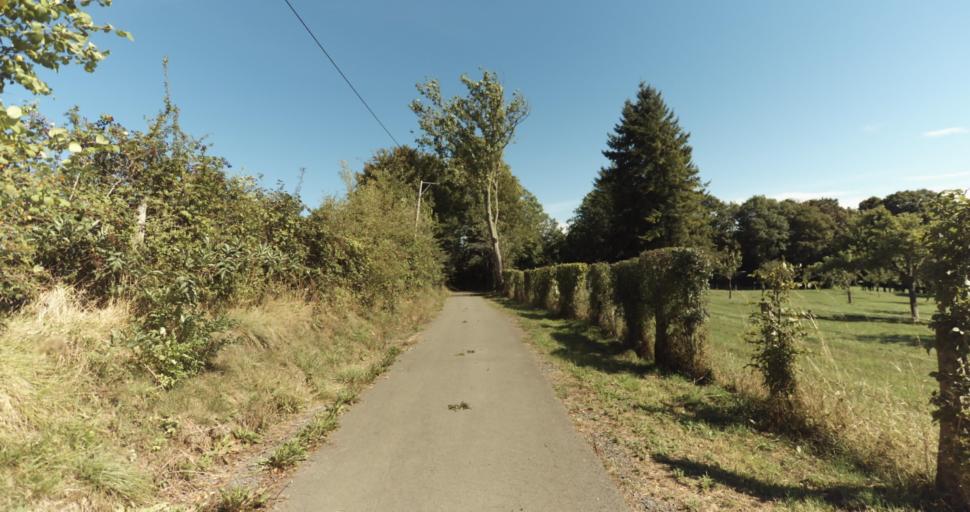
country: FR
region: Lower Normandy
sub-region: Departement de l'Orne
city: Gace
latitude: 48.7923
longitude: 0.2850
